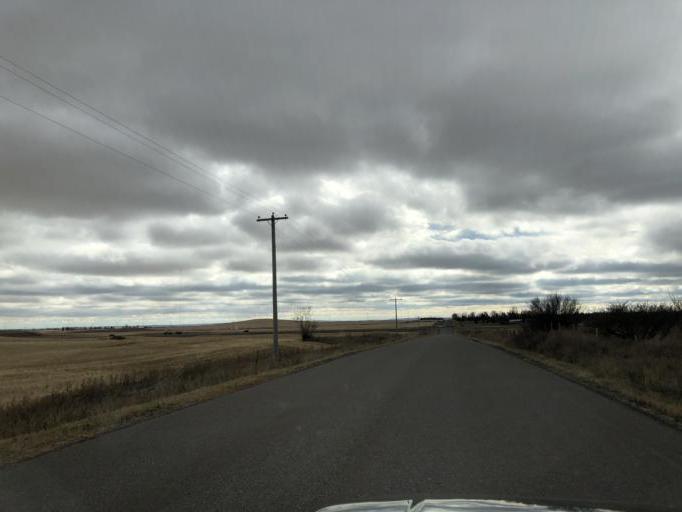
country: CA
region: Alberta
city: Chestermere
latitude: 50.9116
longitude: -113.8829
